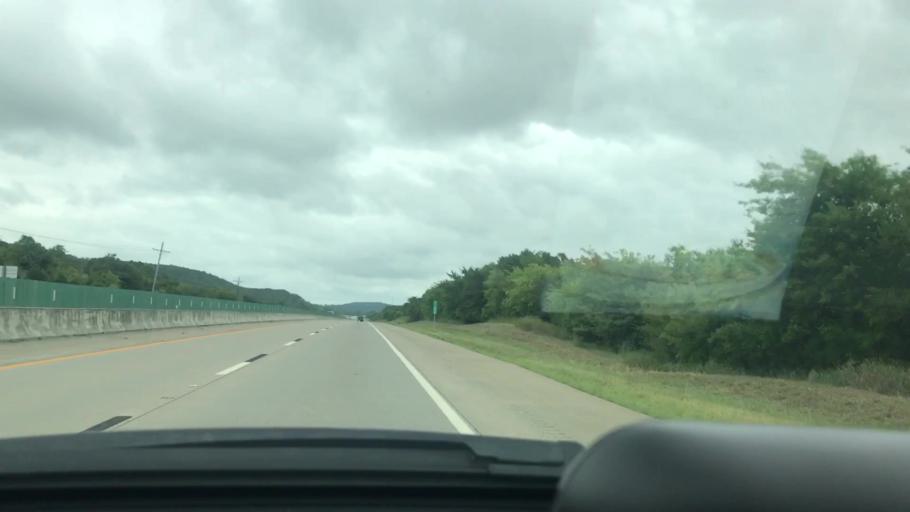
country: US
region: Oklahoma
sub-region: Pittsburg County
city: Krebs
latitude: 35.0744
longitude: -95.7039
